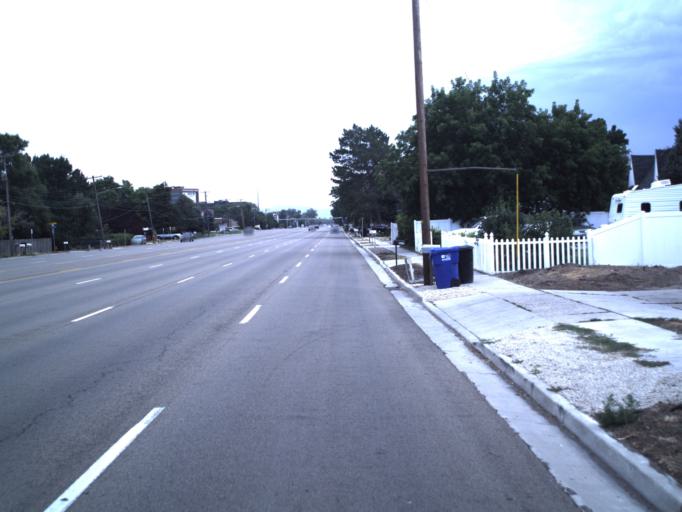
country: US
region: Utah
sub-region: Salt Lake County
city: Millcreek
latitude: 40.6922
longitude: -111.8716
